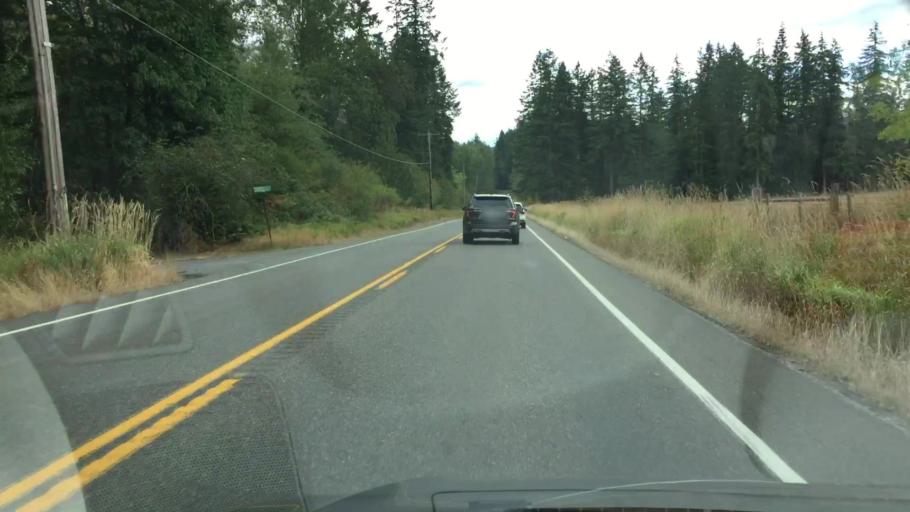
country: US
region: Washington
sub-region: Pierce County
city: Eatonville
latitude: 46.9567
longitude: -122.2974
